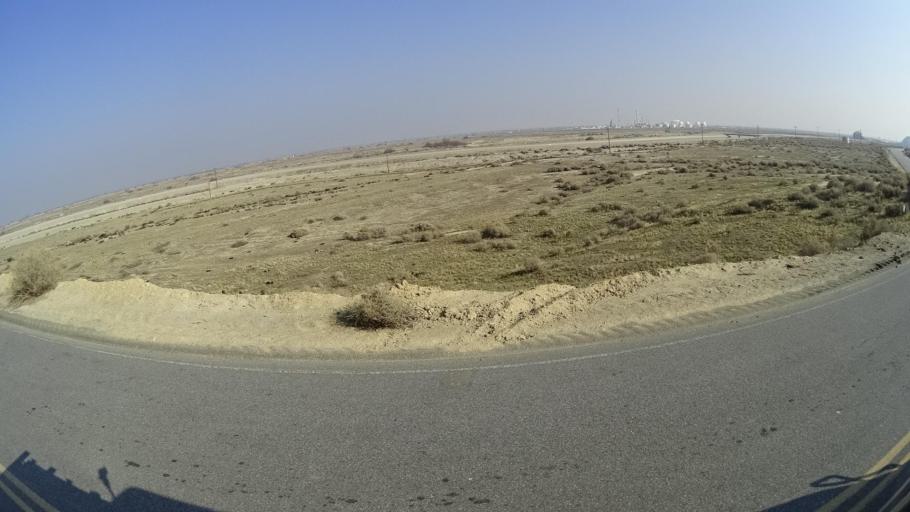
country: US
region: California
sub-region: Kern County
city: Ford City
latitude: 35.2810
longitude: -119.3284
